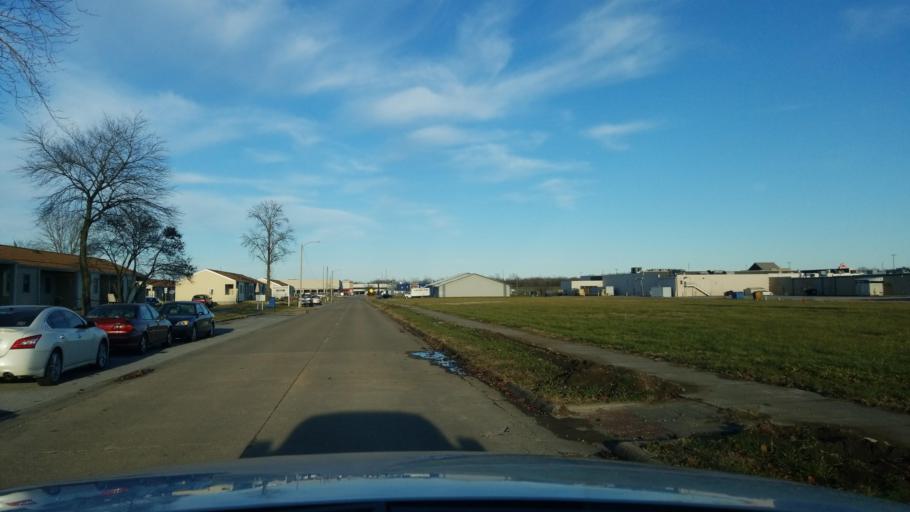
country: US
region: Illinois
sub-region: Saline County
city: Harrisburg
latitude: 37.7451
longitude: -88.5284
